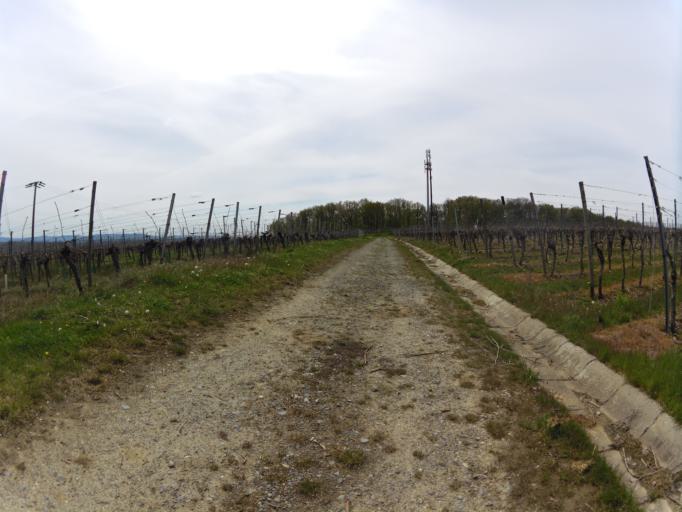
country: DE
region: Bavaria
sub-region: Regierungsbezirk Unterfranken
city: Nordheim
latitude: 49.8596
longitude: 10.1650
